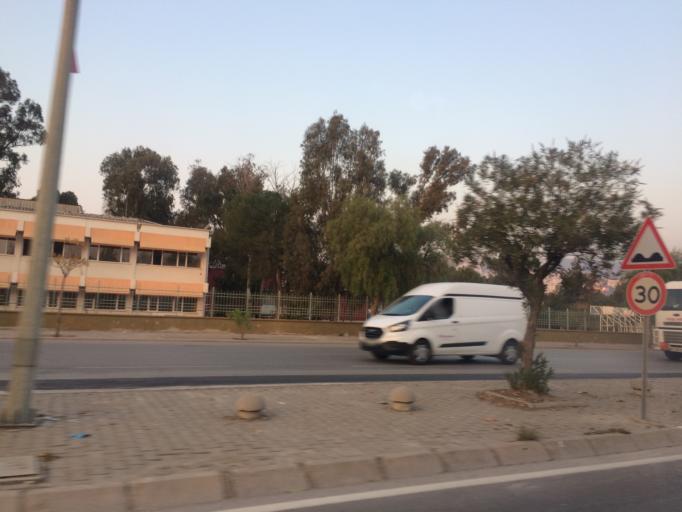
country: TR
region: Izmir
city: Karsiyaka
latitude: 38.4938
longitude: 27.0409
